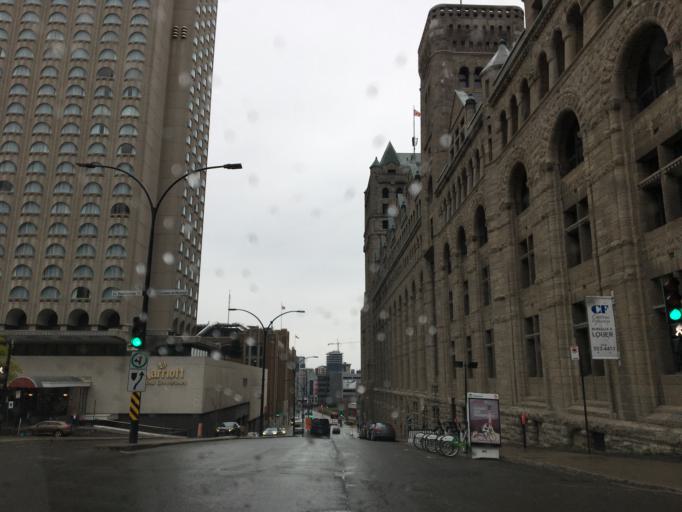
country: CA
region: Quebec
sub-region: Montreal
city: Montreal
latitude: 45.4978
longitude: -73.5688
